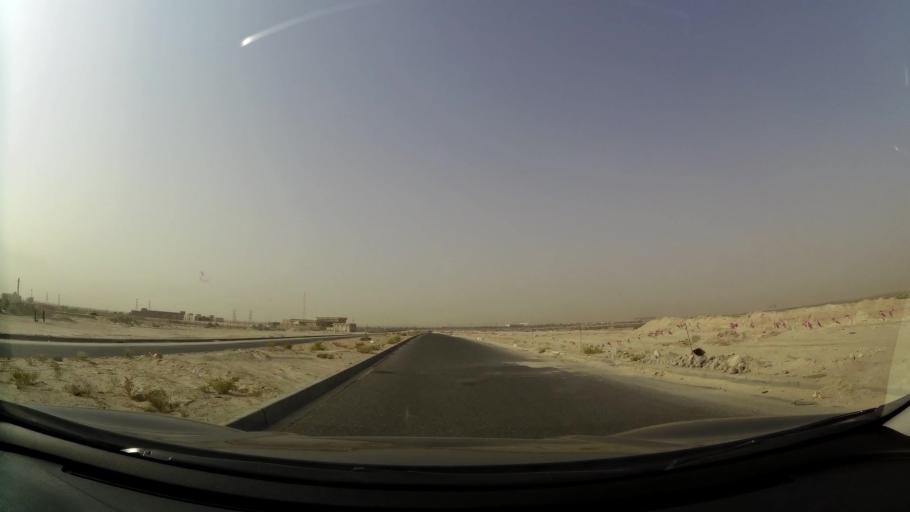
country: KW
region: Muhafazat al Jahra'
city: Al Jahra'
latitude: 29.3512
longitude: 47.7389
